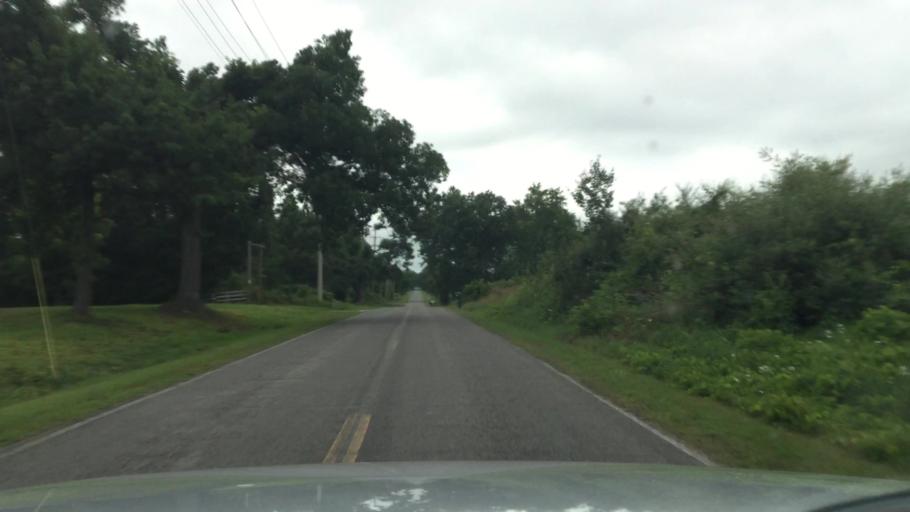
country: US
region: Michigan
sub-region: Montcalm County
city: Greenville
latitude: 43.1828
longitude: -85.2233
